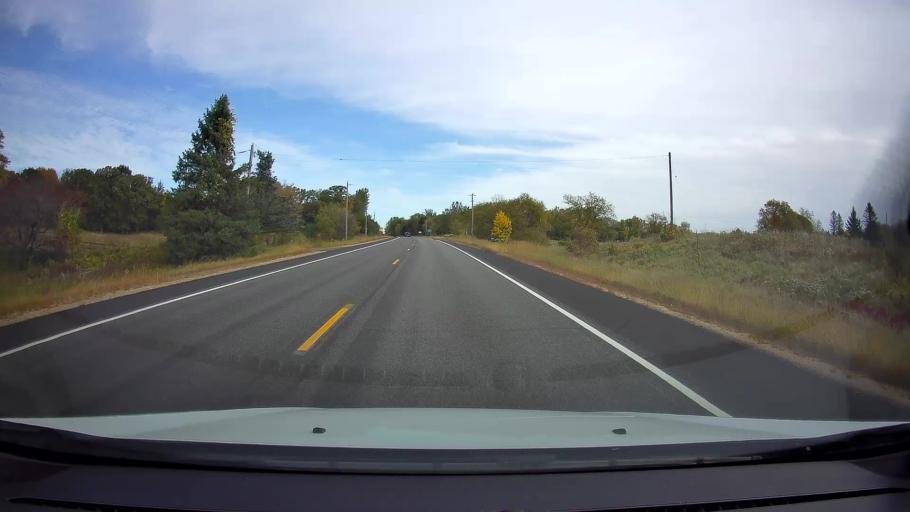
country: US
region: Minnesota
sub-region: Washington County
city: Stillwater
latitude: 45.1255
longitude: -92.7647
